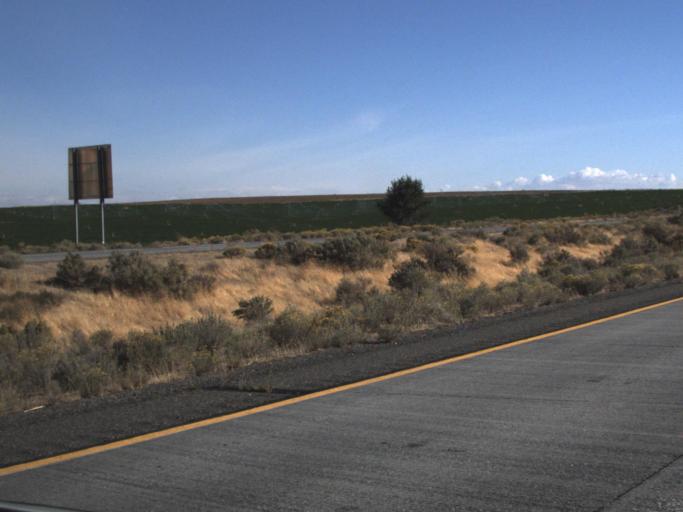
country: US
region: Washington
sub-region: Benton County
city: West Richland
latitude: 46.2135
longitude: -119.3455
